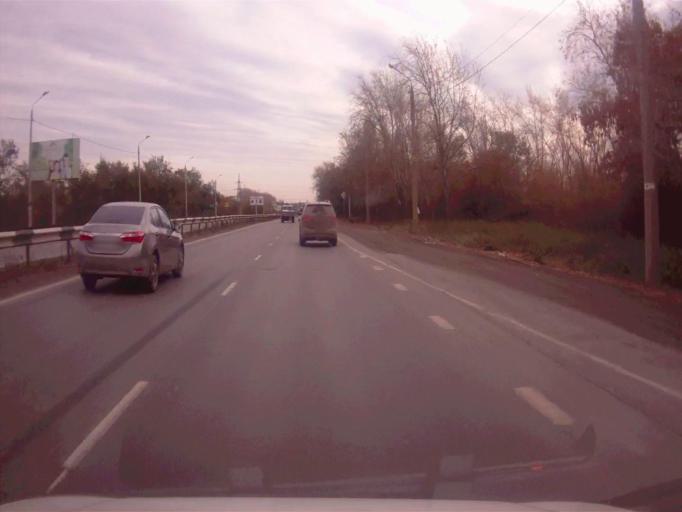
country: RU
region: Chelyabinsk
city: Novosineglazovskiy
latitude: 55.0530
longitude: 61.4102
